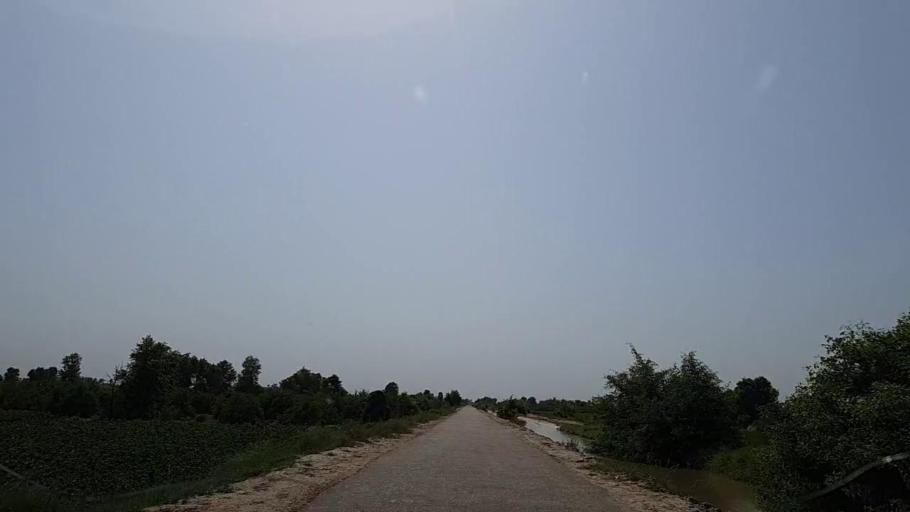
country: PK
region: Sindh
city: Kandiaro
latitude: 27.0504
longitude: 68.1610
